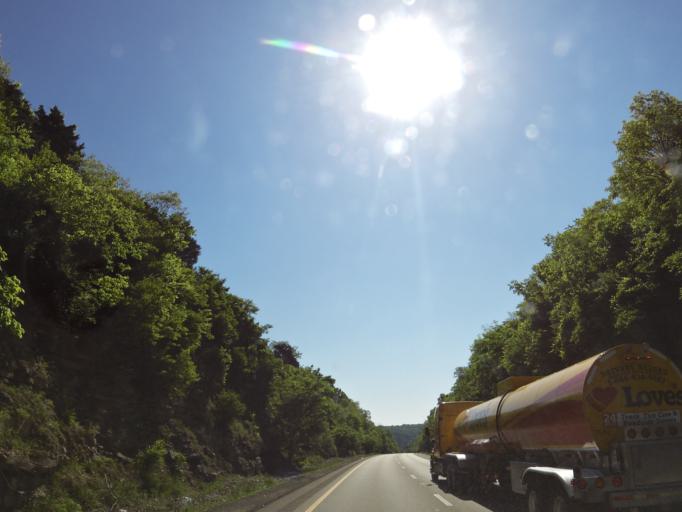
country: US
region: Kentucky
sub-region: Franklin County
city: Frankfort
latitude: 38.1584
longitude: -84.8700
